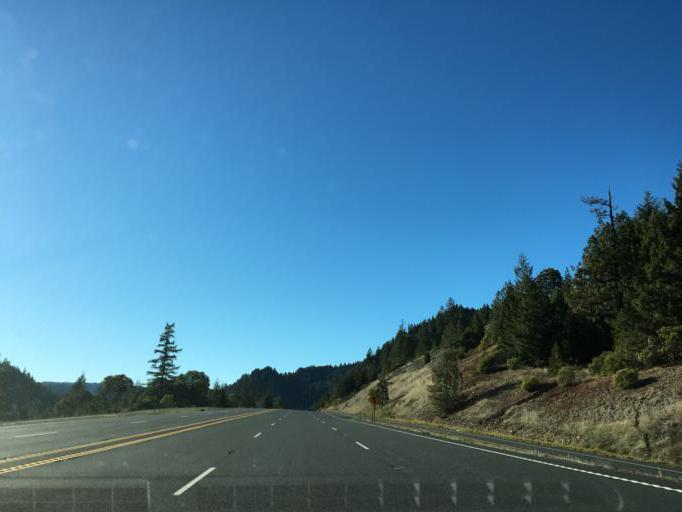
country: US
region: California
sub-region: Mendocino County
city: Laytonville
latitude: 39.8346
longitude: -123.6331
